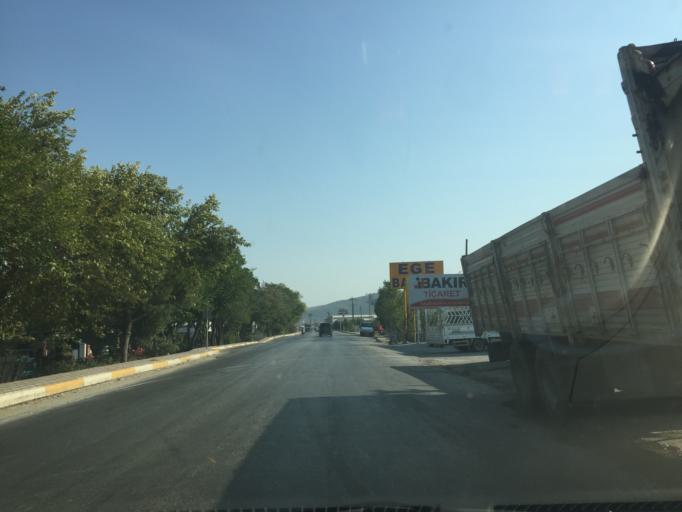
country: TR
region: Manisa
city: Akhisar
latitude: 38.9057
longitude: 27.8368
